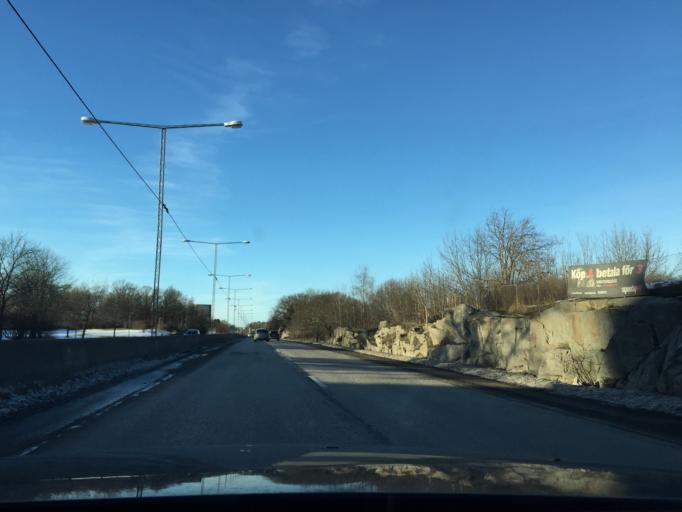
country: SE
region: Stockholm
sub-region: Stockholms Kommun
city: Bromma
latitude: 59.3551
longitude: 17.8791
